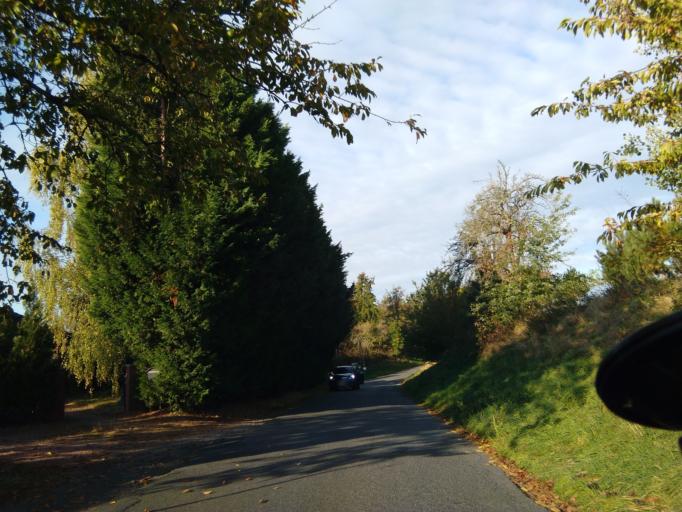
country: DE
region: Saxony
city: Meissen
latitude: 51.1846
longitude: 13.4710
